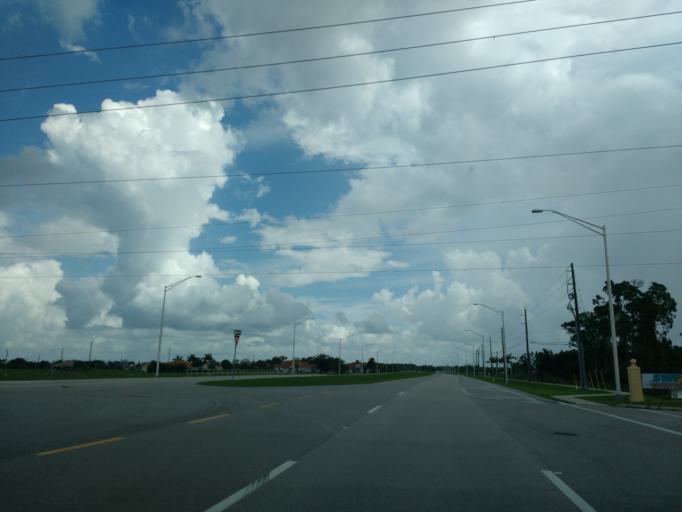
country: US
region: Florida
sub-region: Lee County
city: Burnt Store Marina
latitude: 26.7866
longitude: -82.0379
